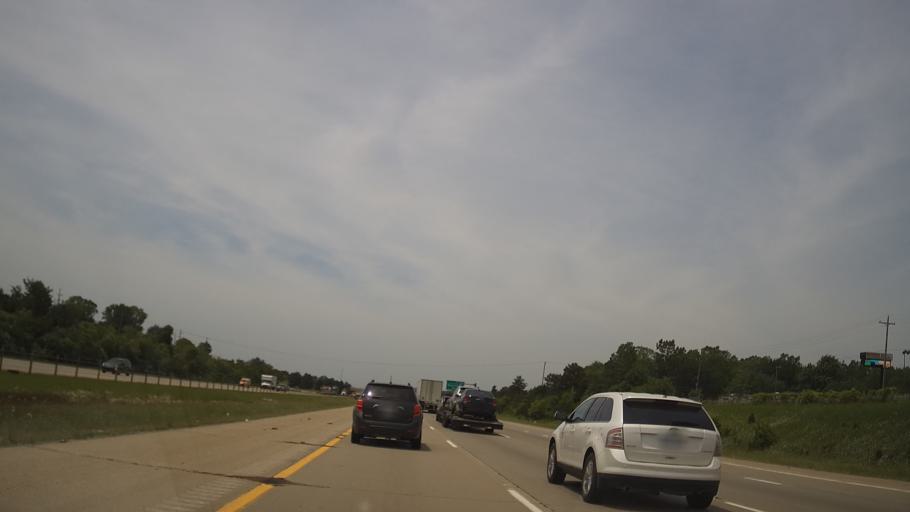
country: US
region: Michigan
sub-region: Wayne County
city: Belleville
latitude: 42.2200
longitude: -83.4759
